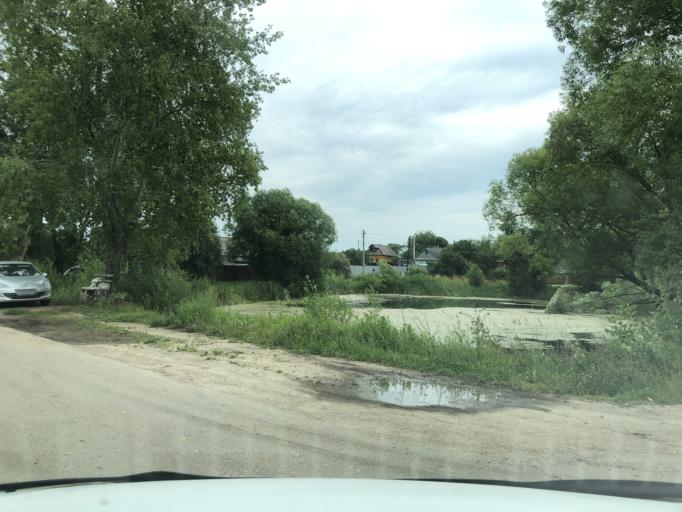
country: RU
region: Jaroslavl
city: Petrovsk
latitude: 57.0069
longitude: 39.2634
